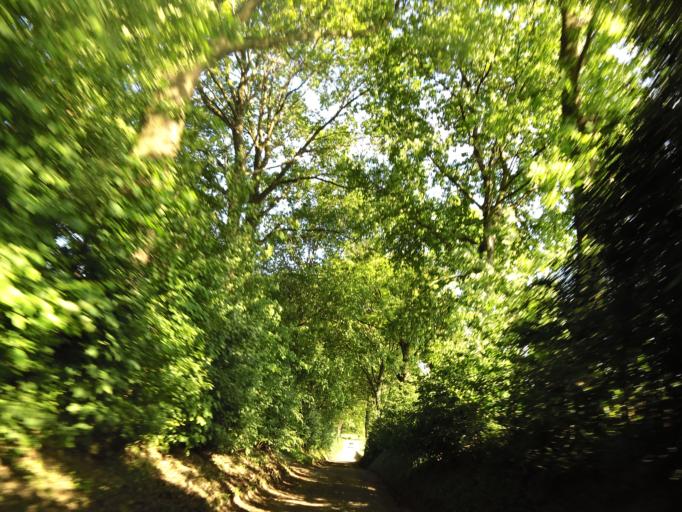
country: NL
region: Limburg
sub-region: Gemeente Voerendaal
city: Ubachsberg
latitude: 50.8465
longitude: 5.9197
